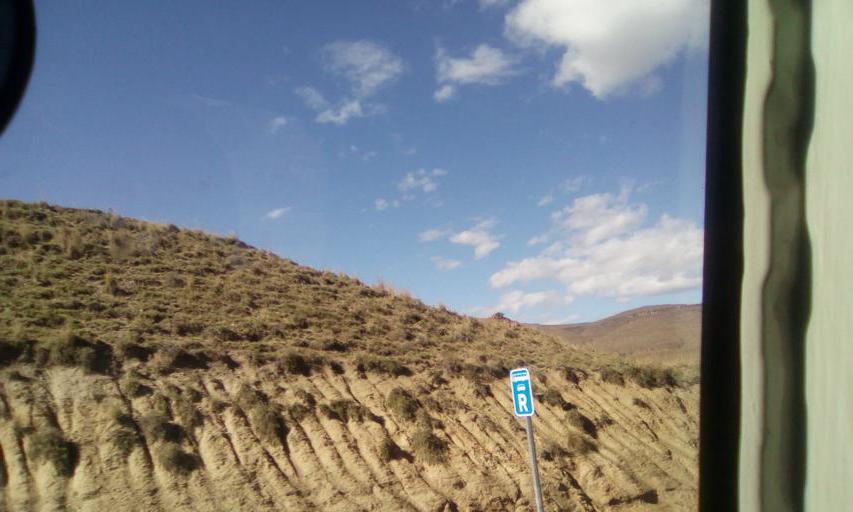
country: LS
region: Qacha's Nek
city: Qacha's Nek
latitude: -30.0399
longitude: 28.2557
